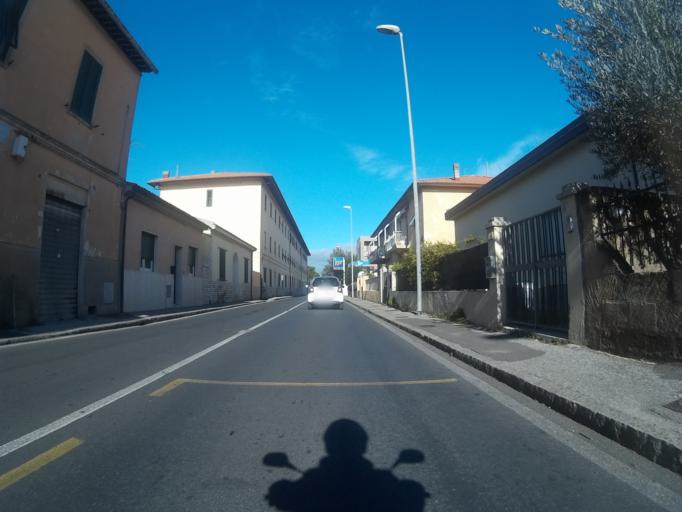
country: IT
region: Tuscany
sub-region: Provincia di Livorno
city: Livorno
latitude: 43.5361
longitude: 10.3419
